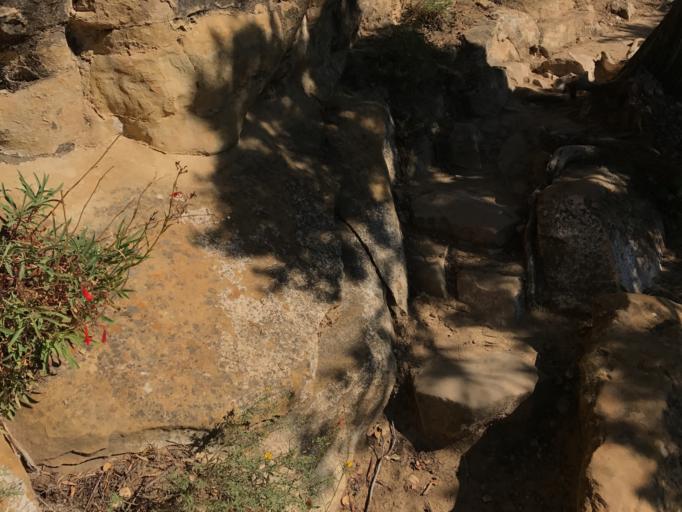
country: US
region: Colorado
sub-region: Montezuma County
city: Cortez
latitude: 37.1817
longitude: -108.4882
